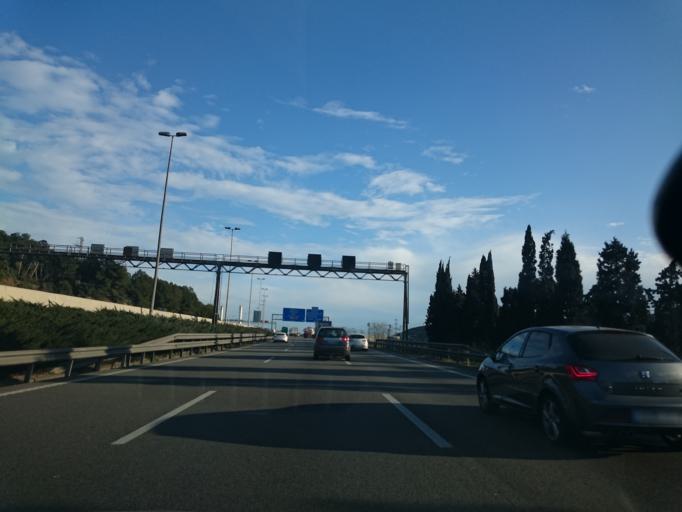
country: ES
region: Catalonia
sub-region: Provincia de Barcelona
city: Sant Andreu de la Barca
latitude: 41.4533
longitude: 1.9838
